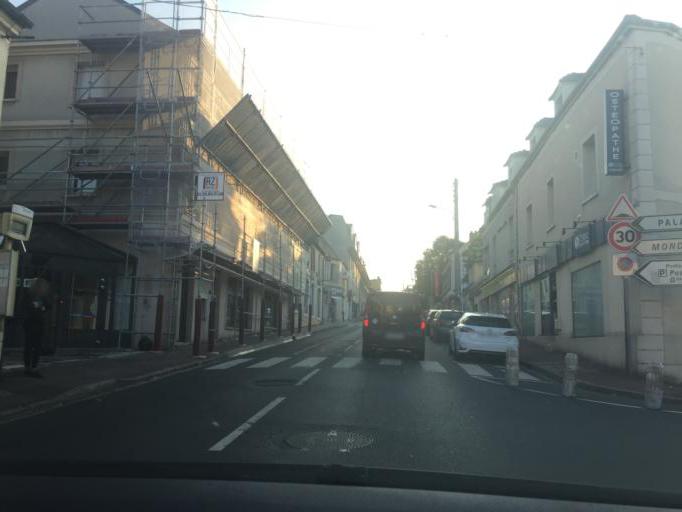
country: FR
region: Ile-de-France
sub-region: Departement de l'Essonne
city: Orsay
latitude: 48.6984
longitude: 2.1874
